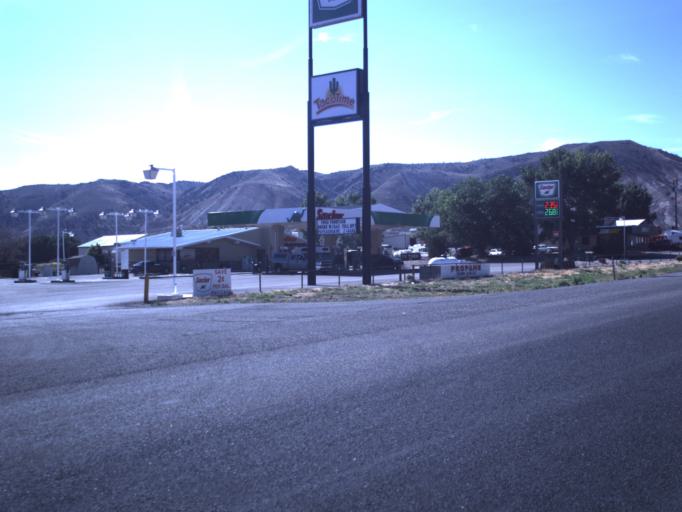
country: US
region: Utah
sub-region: Sevier County
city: Salina
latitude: 38.9391
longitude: -111.8546
